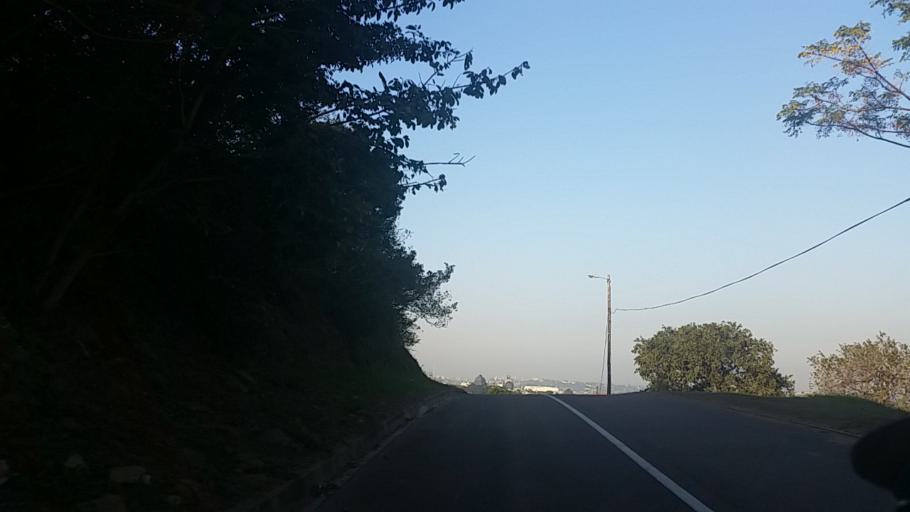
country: ZA
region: KwaZulu-Natal
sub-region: eThekwini Metropolitan Municipality
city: Berea
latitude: -29.8494
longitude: 30.9212
